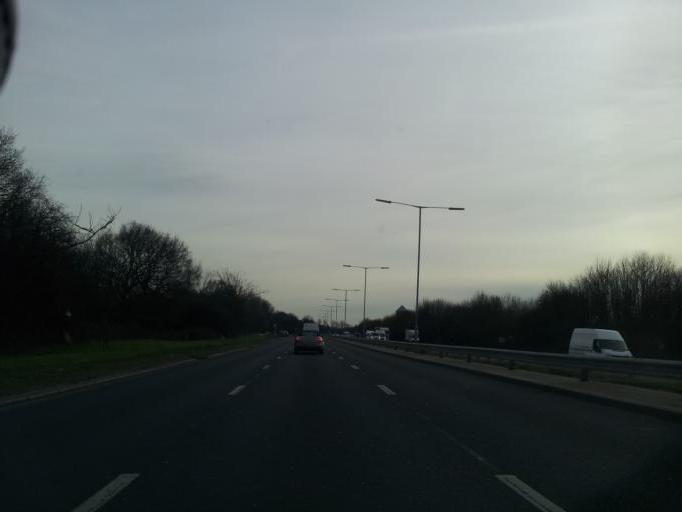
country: GB
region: England
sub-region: Hertfordshire
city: Borehamwood
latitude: 51.6523
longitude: -0.2500
